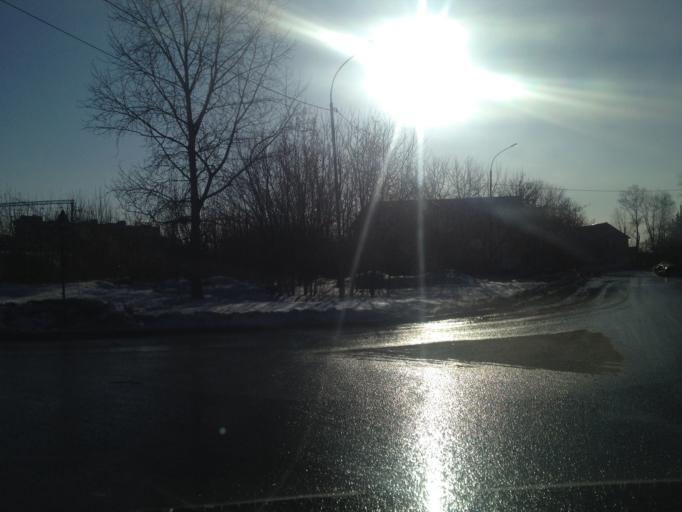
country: RU
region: Sverdlovsk
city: Yekaterinburg
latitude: 56.8600
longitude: 60.5819
